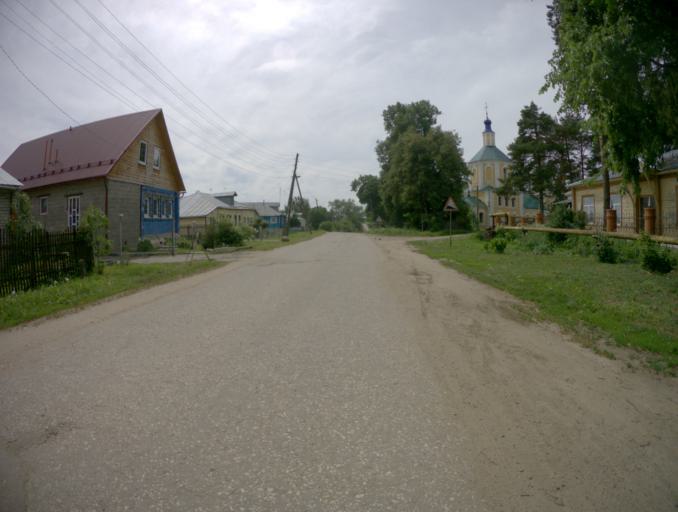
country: RU
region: Vladimir
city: Stavrovo
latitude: 56.1688
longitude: 39.9729
